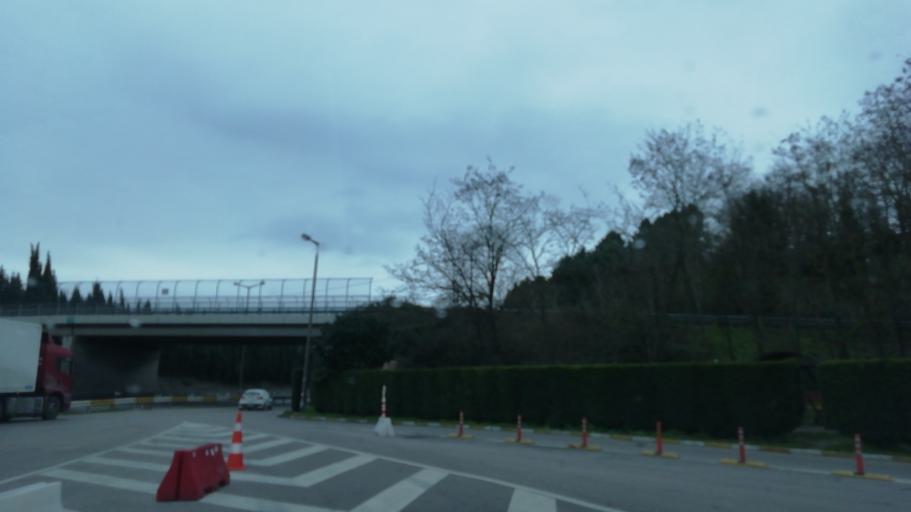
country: TR
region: Sakarya
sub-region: Merkez
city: Sapanca
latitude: 40.7036
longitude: 30.3133
